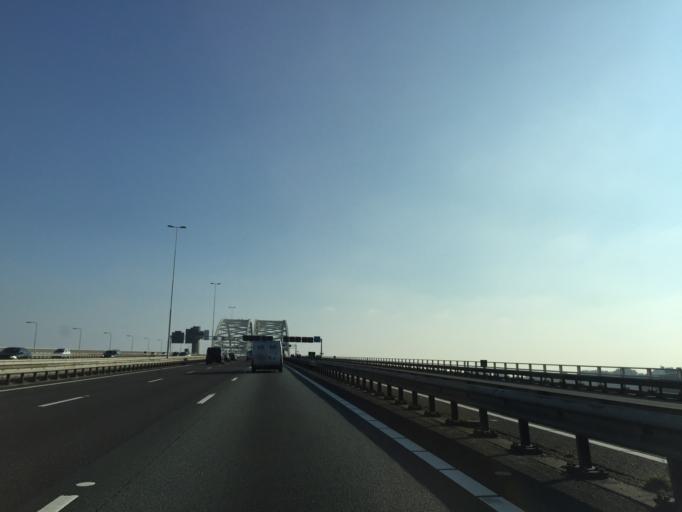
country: NL
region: South Holland
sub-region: Gemeente Rotterdam
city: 's-Gravenland
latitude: 51.9083
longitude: 4.5395
